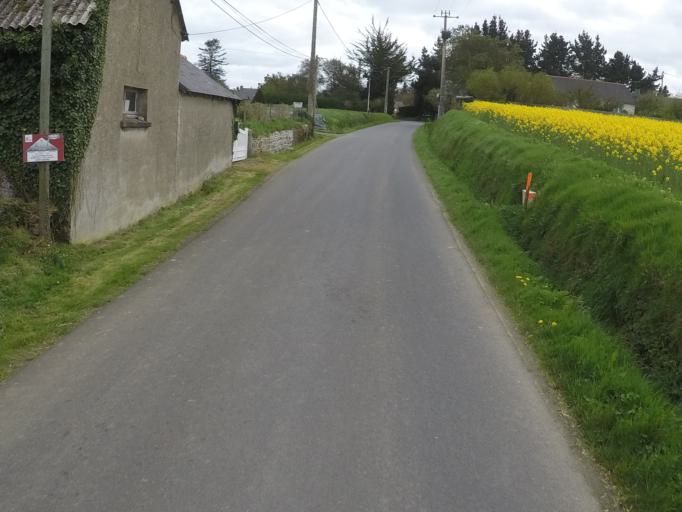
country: FR
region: Brittany
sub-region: Departement des Cotes-d'Armor
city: Plouha
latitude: 48.6644
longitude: -2.9207
